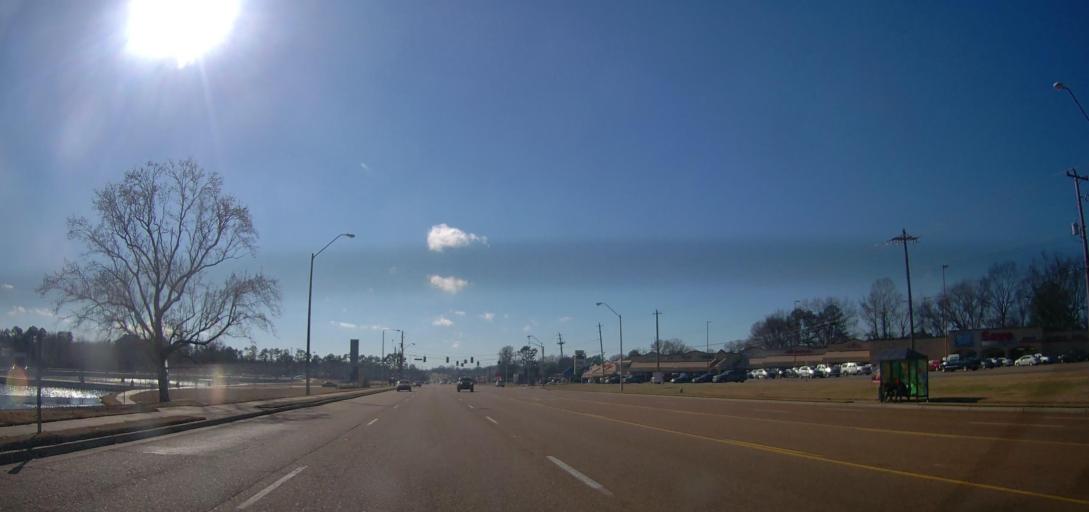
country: US
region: Tennessee
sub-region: Shelby County
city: Bartlett
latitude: 35.2203
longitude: -89.9099
